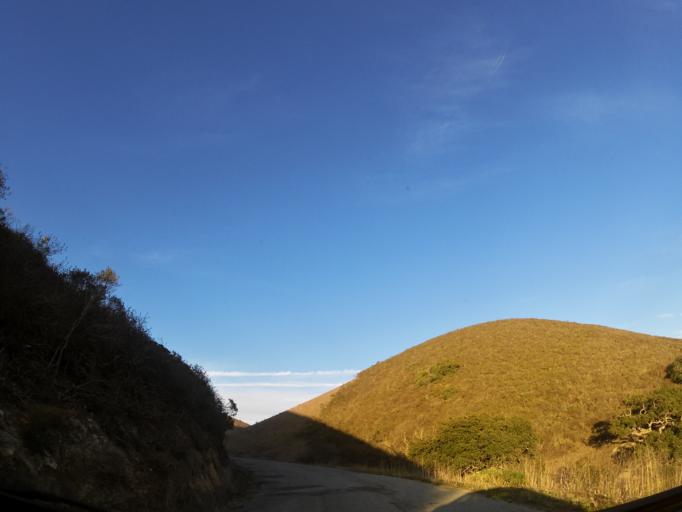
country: US
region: California
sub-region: San Benito County
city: San Juan Bautista
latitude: 36.8186
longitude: -121.5750
